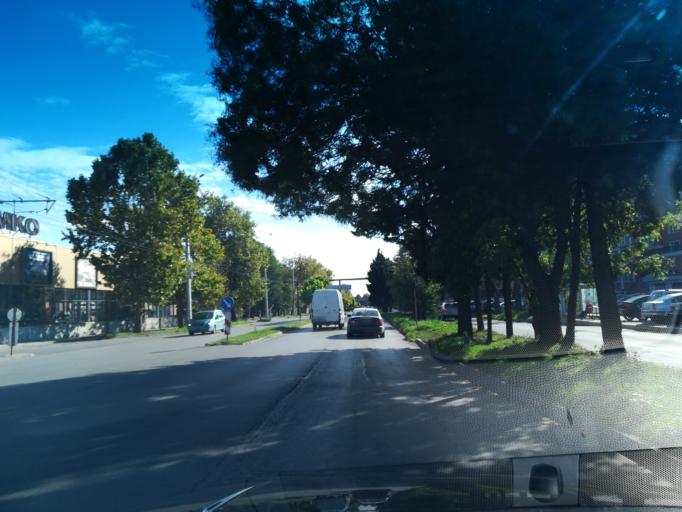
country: BG
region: Stara Zagora
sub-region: Obshtina Stara Zagora
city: Stara Zagora
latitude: 42.4132
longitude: 25.6387
